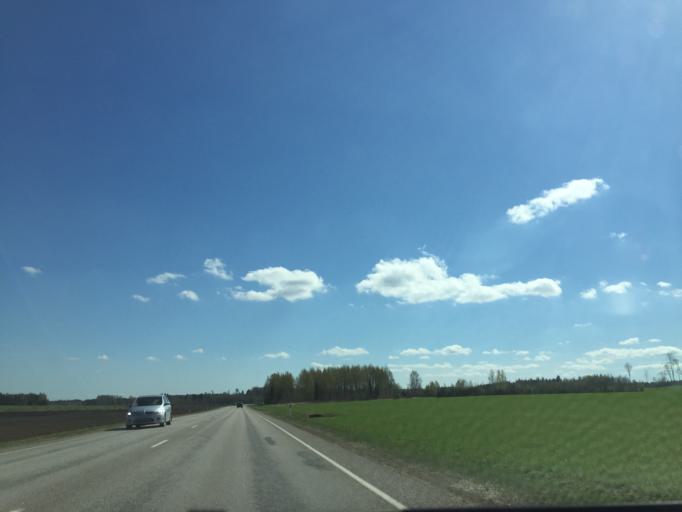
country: EE
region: Valgamaa
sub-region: Valga linn
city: Valga
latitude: 57.8797
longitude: 26.0597
